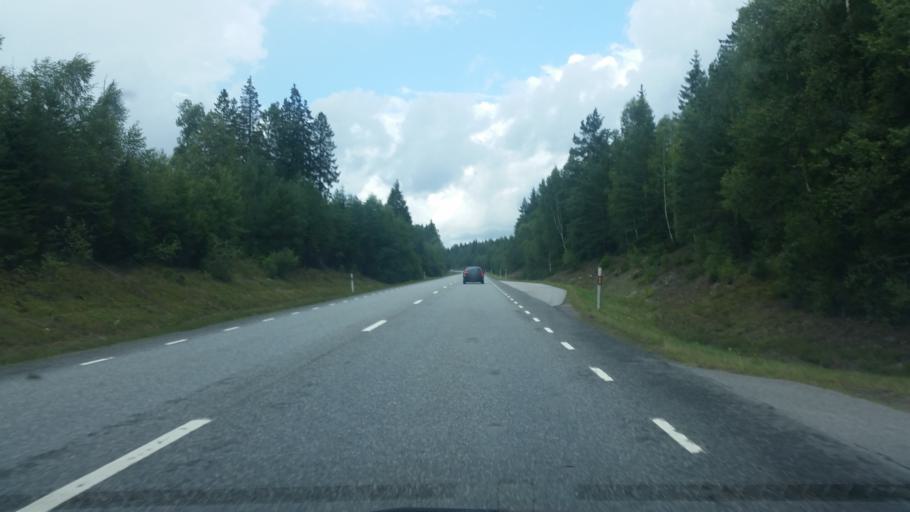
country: SE
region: Vaestra Goetaland
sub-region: Tranemo Kommun
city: Langhem
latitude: 57.5954
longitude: 13.1873
